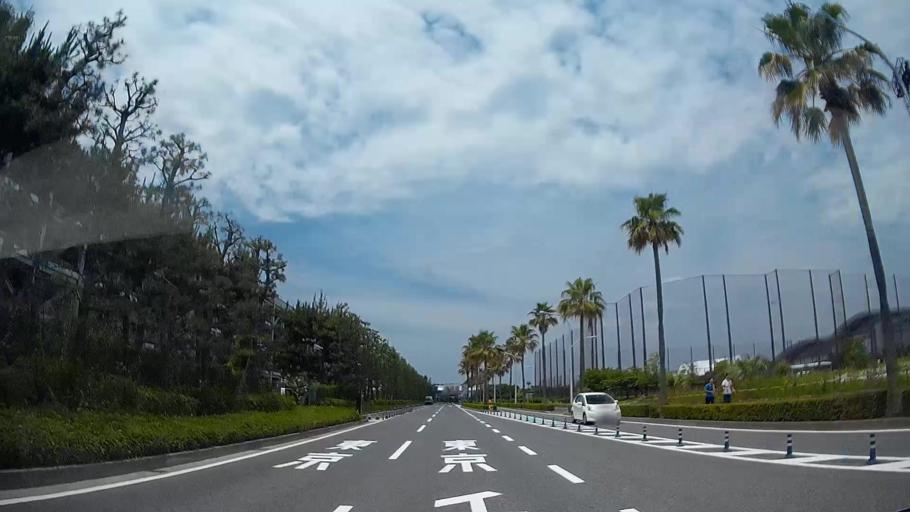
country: JP
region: Tokyo
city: Urayasu
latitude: 35.6274
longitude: 139.8913
